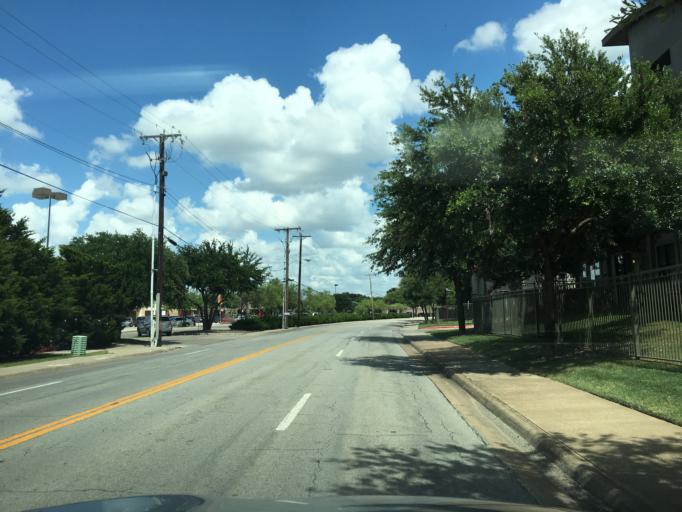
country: US
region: Texas
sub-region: Dallas County
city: Highland Park
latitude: 32.8562
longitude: -96.7543
